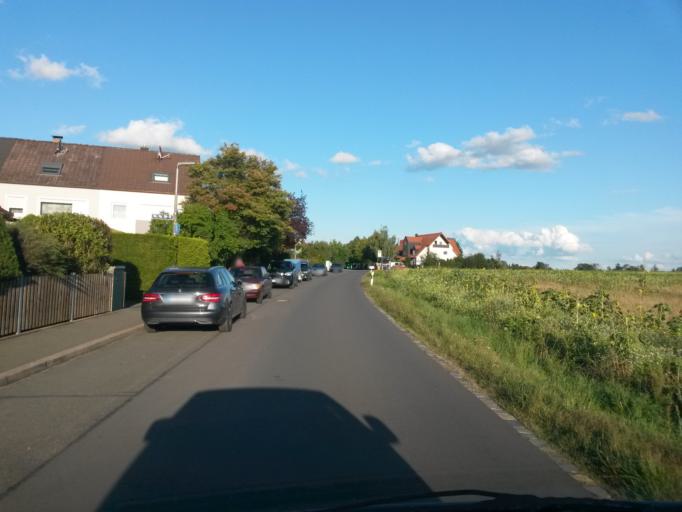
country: DE
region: Bavaria
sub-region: Regierungsbezirk Mittelfranken
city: Furth
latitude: 49.5269
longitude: 11.0187
